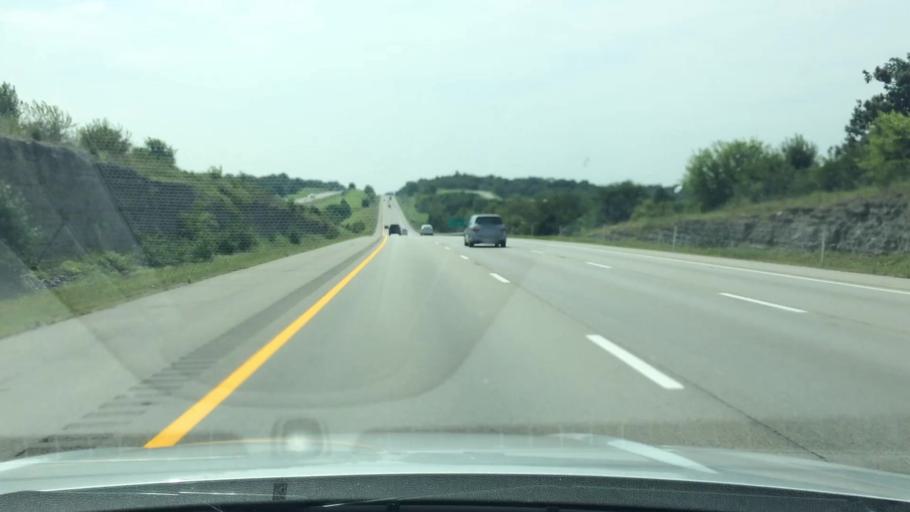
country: US
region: Kentucky
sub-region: Madison County
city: Richmond
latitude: 37.7253
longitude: -84.3237
